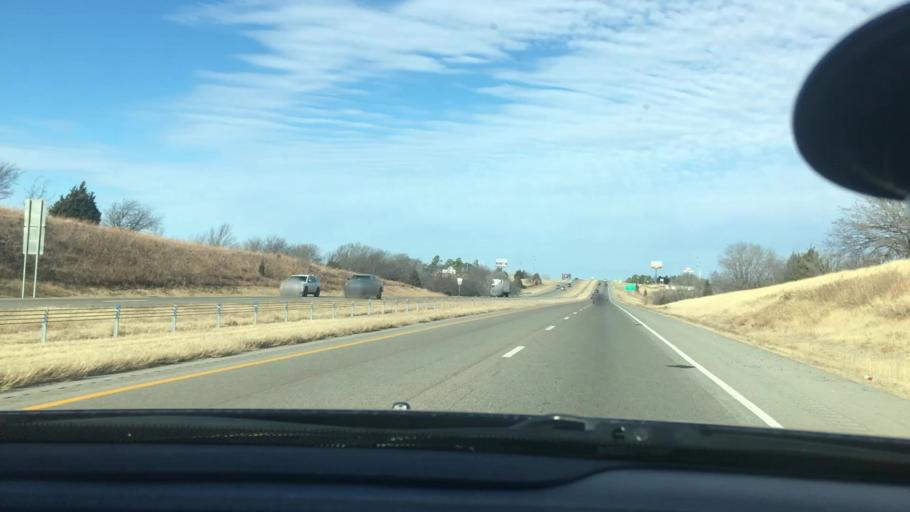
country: US
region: Oklahoma
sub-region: Cleveland County
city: Noble
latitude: 35.0725
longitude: -97.4013
